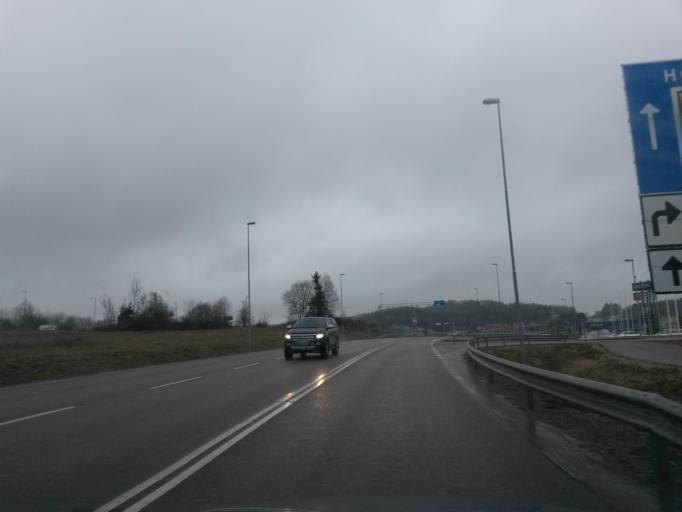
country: SE
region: Vaestra Goetaland
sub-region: Uddevalla Kommun
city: Uddevalla
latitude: 58.3516
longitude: 11.8250
